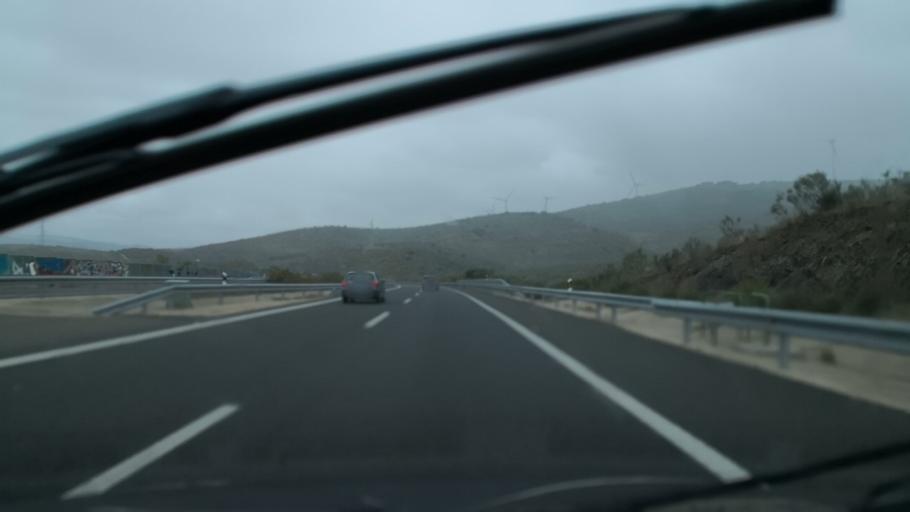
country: ES
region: Extremadura
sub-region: Provincia de Caceres
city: Plasencia
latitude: 40.0075
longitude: -6.1382
